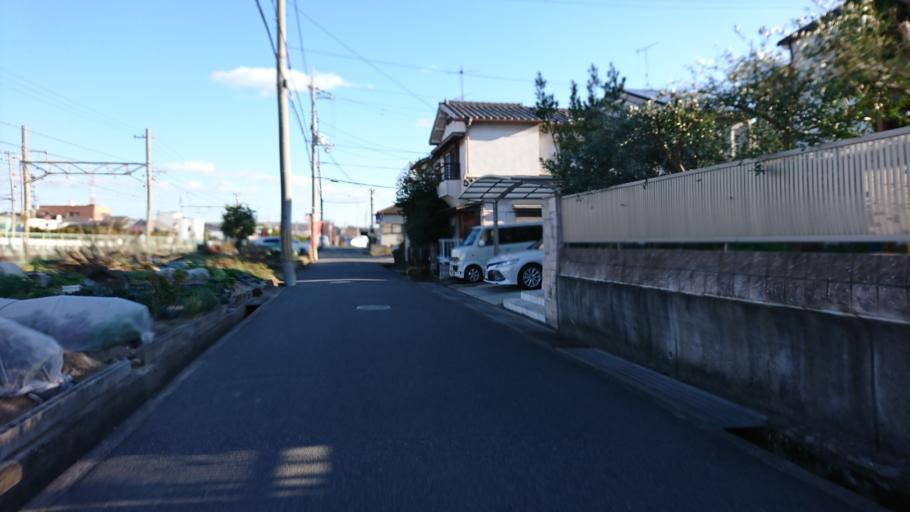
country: JP
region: Hyogo
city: Kakogawacho-honmachi
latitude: 34.7511
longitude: 134.8164
